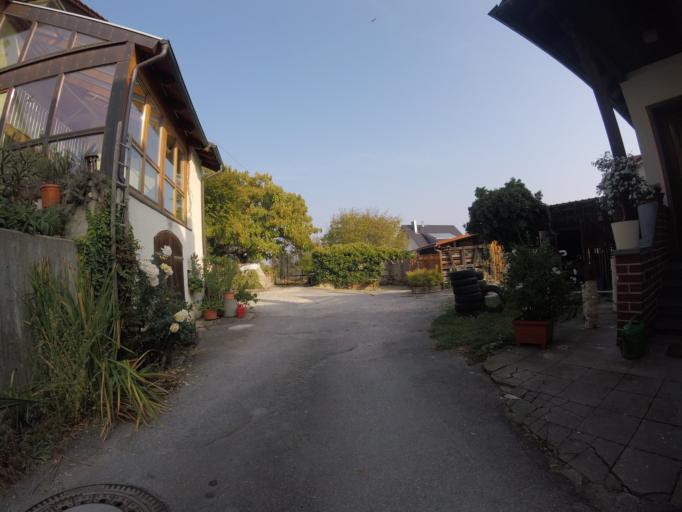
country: DE
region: Baden-Wuerttemberg
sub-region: Regierungsbezirk Stuttgart
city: Mittelschontal
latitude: 48.9464
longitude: 9.3950
